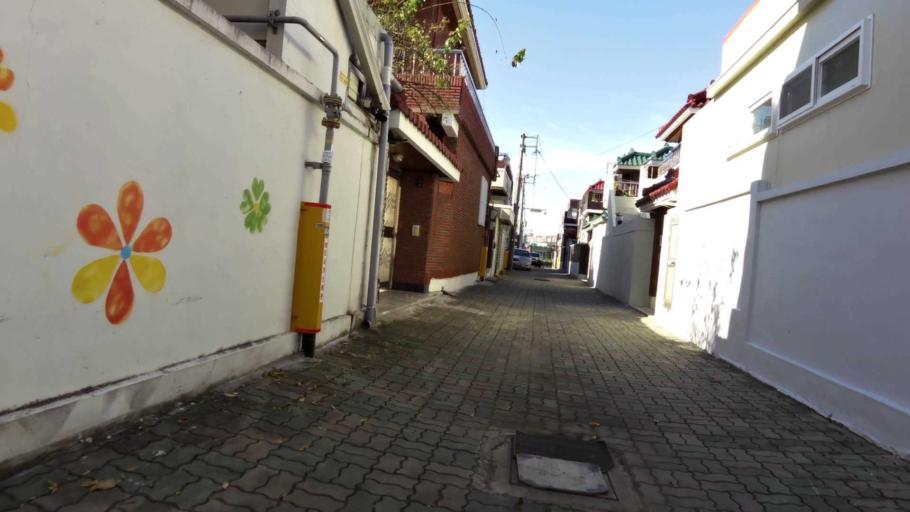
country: KR
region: Daegu
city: Daegu
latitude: 35.8623
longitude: 128.6432
